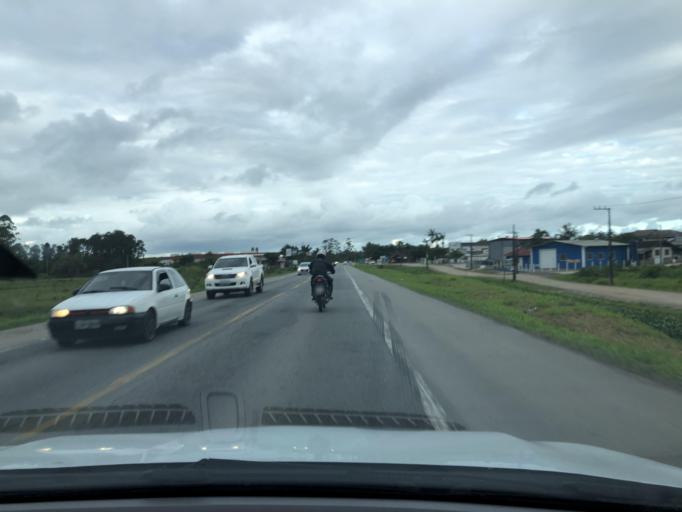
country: BR
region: Santa Catarina
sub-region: Joinville
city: Joinville
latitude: -26.4139
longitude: -48.7608
